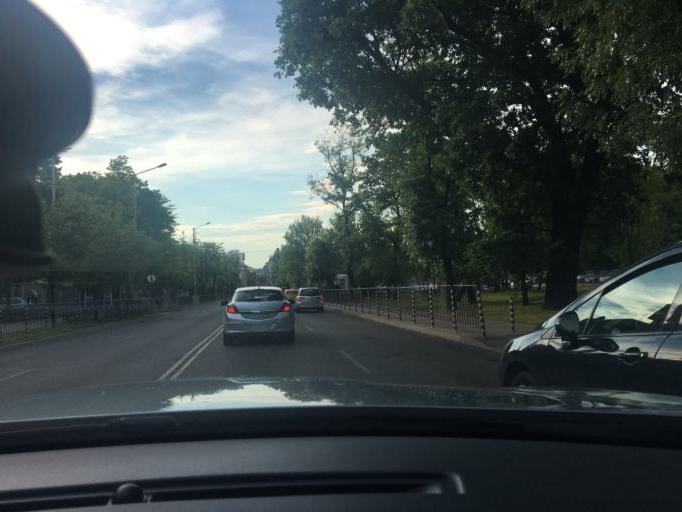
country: BG
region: Sofia-Capital
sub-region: Stolichna Obshtina
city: Sofia
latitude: 42.6844
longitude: 23.3333
